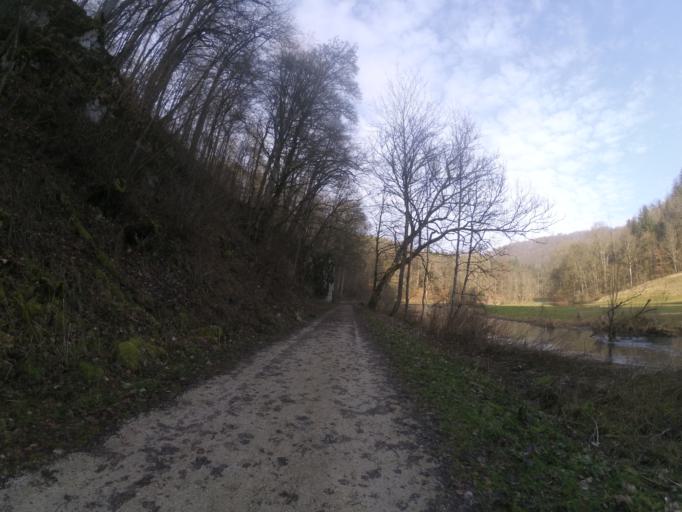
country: DE
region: Baden-Wuerttemberg
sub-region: Tuebingen Region
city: Emeringen
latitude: 48.2711
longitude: 9.5193
